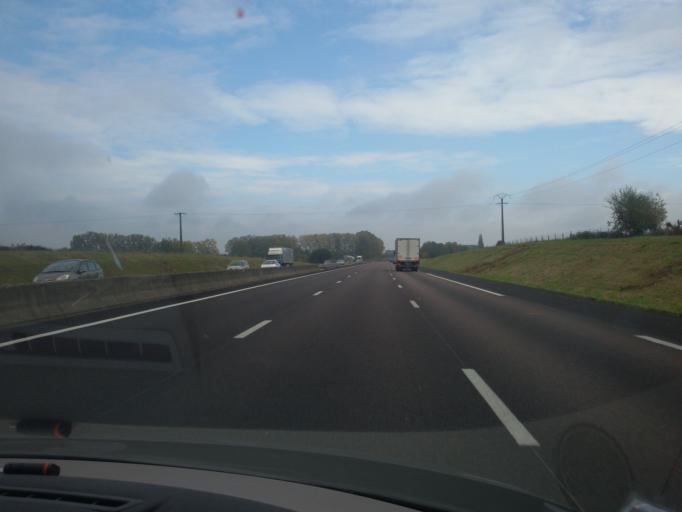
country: FR
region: Haute-Normandie
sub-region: Departement de l'Eure
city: Hauville
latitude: 49.3694
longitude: 0.7715
